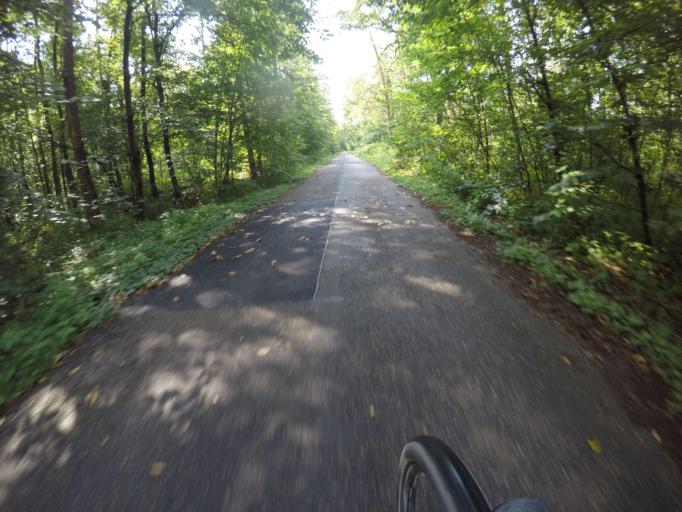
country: DE
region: Baden-Wuerttemberg
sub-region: Karlsruhe Region
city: Oftersheim
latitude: 49.3527
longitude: 8.5565
